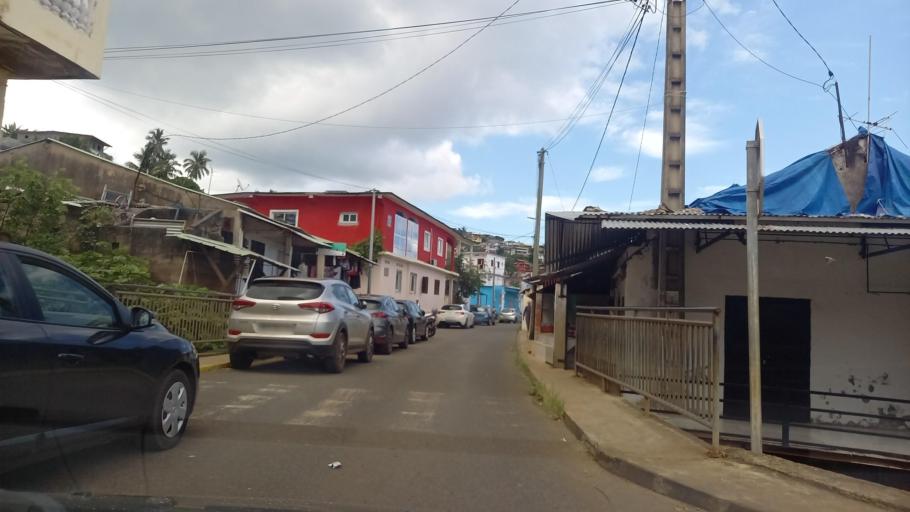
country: YT
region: Sada
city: Sada
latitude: -12.8480
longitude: 45.1005
